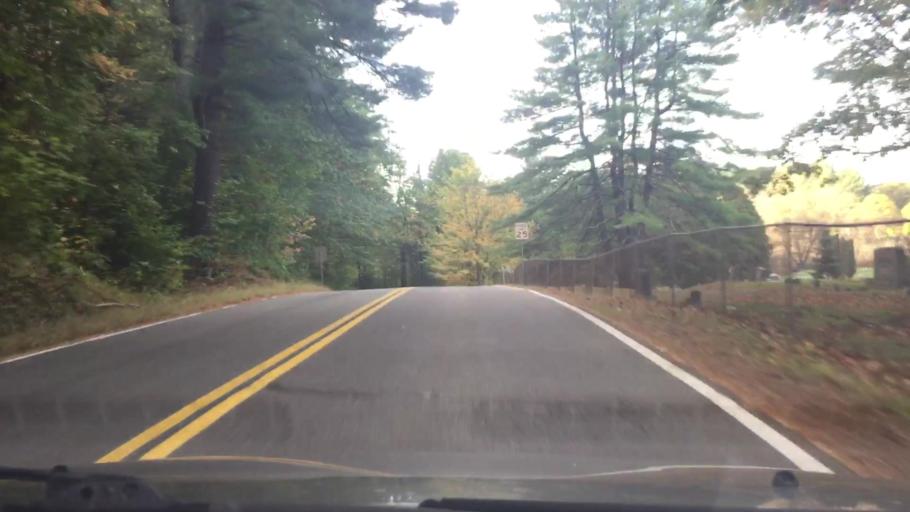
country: US
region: New Hampshire
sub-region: Cheshire County
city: Keene
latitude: 42.9421
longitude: -72.2668
